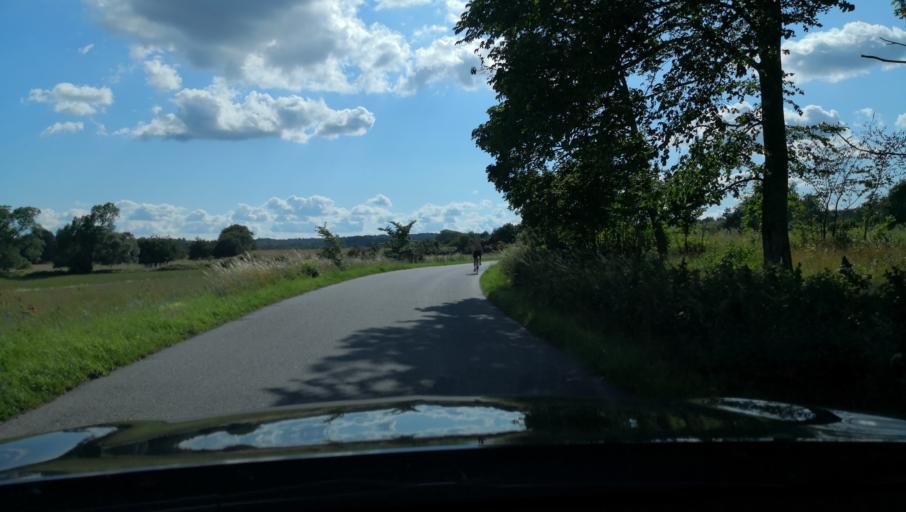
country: SE
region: Skane
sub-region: Kristianstads Kommun
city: Degeberga
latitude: 55.7680
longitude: 14.1569
